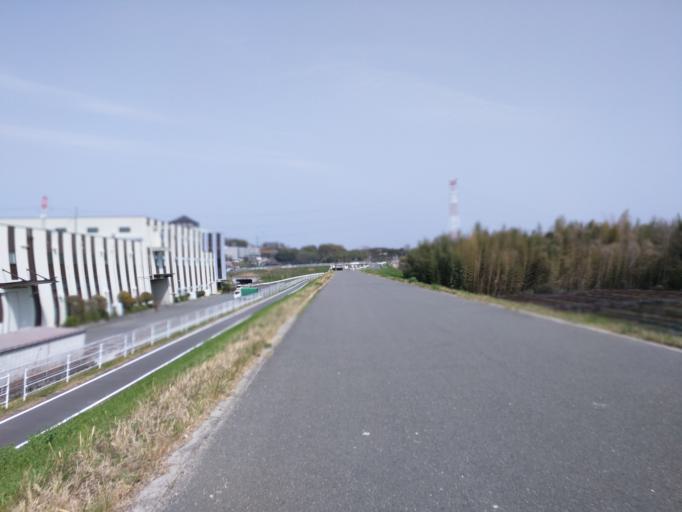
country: JP
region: Kyoto
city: Tanabe
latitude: 34.7968
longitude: 135.7946
